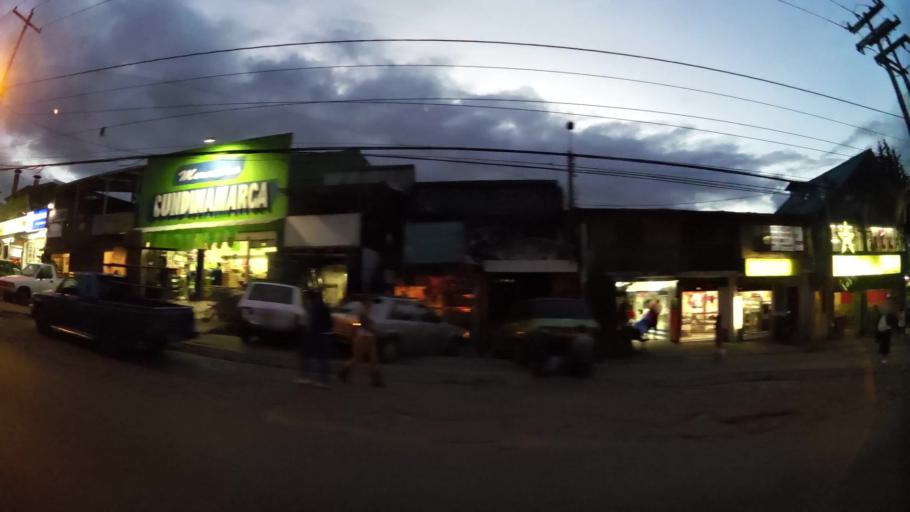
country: CO
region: Bogota D.C.
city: Bogota
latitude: 4.5512
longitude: -74.0863
